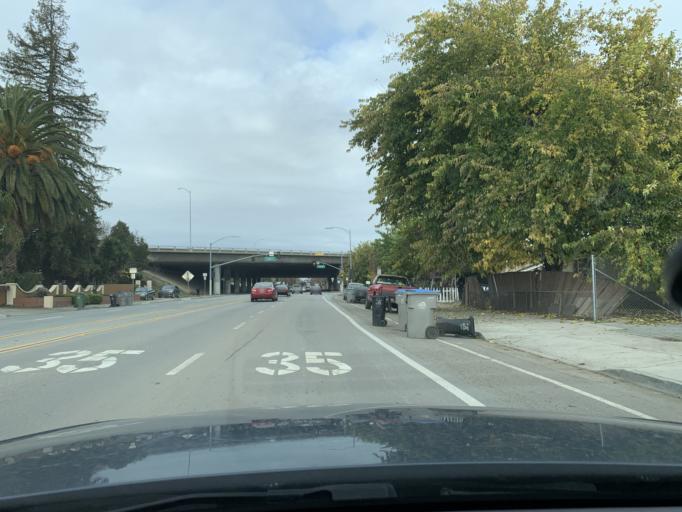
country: US
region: California
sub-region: Santa Clara County
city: Alum Rock
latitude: 37.3514
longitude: -121.8367
